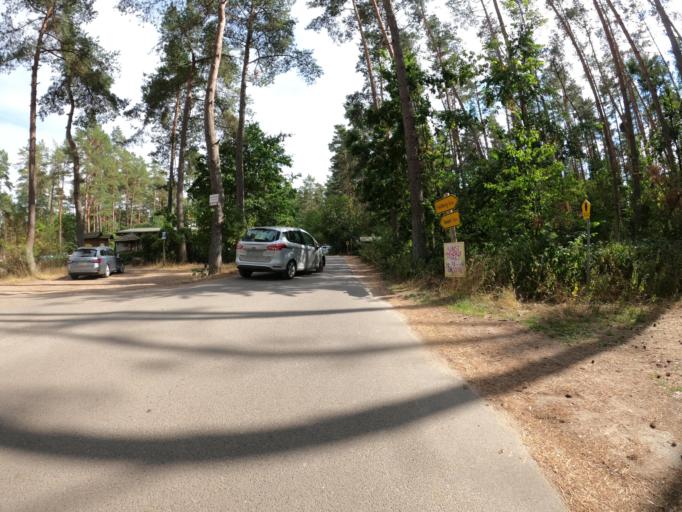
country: DE
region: Brandenburg
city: Lychen
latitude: 53.2832
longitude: 13.4294
